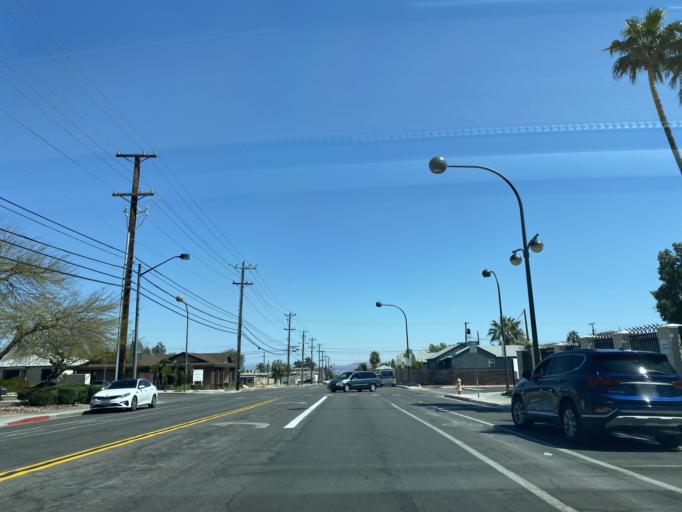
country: US
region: Nevada
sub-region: Clark County
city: Las Vegas
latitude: 36.1651
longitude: -115.1381
